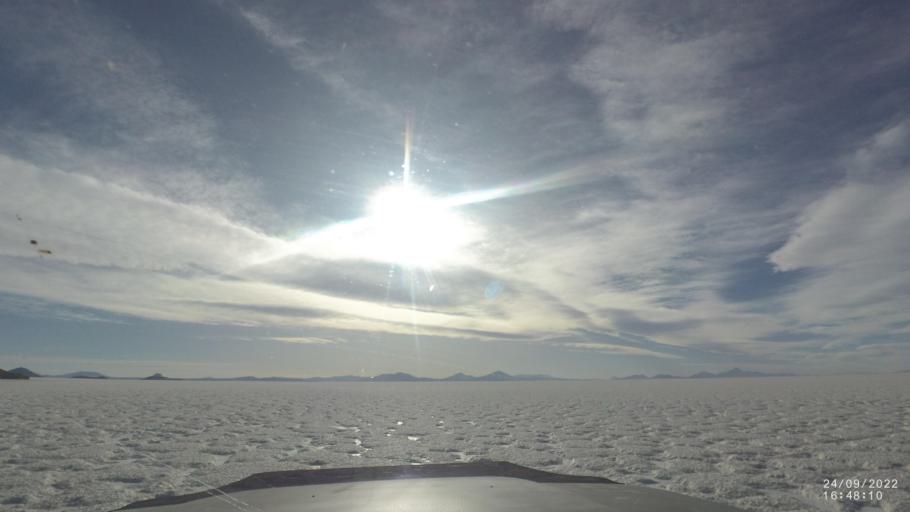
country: BO
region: Potosi
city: Colchani
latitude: -20.1325
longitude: -67.8088
